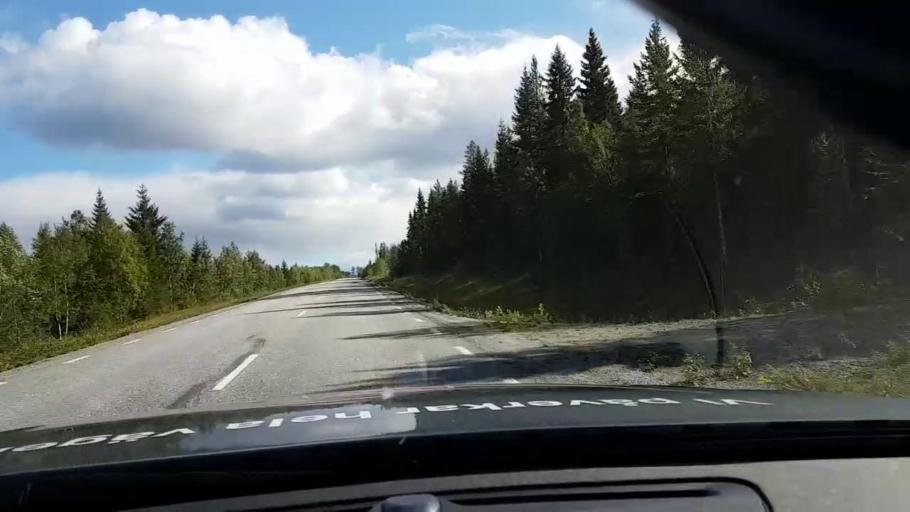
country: SE
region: Vaesterbotten
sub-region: Asele Kommun
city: Asele
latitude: 63.7798
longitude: 17.6655
